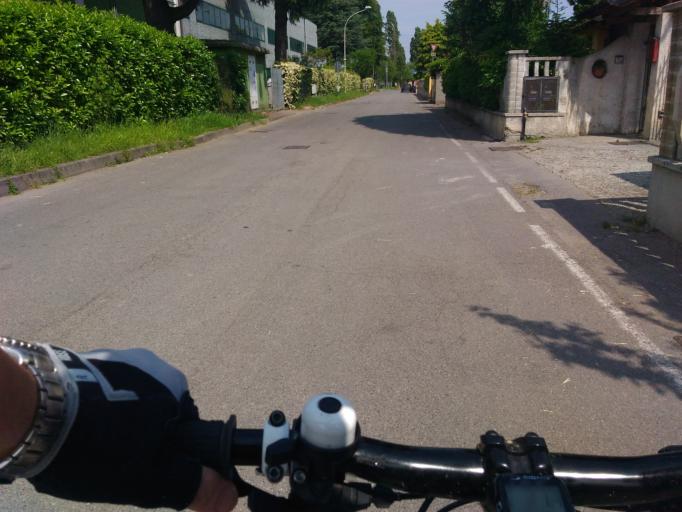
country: IT
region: Lombardy
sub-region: Provincia di Lodi
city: Casalmaiocco
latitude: 45.3576
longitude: 9.3667
